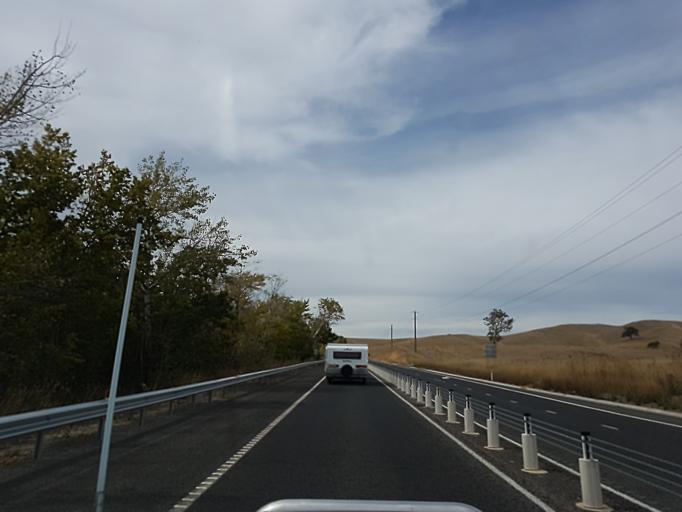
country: AU
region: Victoria
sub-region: Murrindindi
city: Alexandra
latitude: -37.1936
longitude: 145.4829
